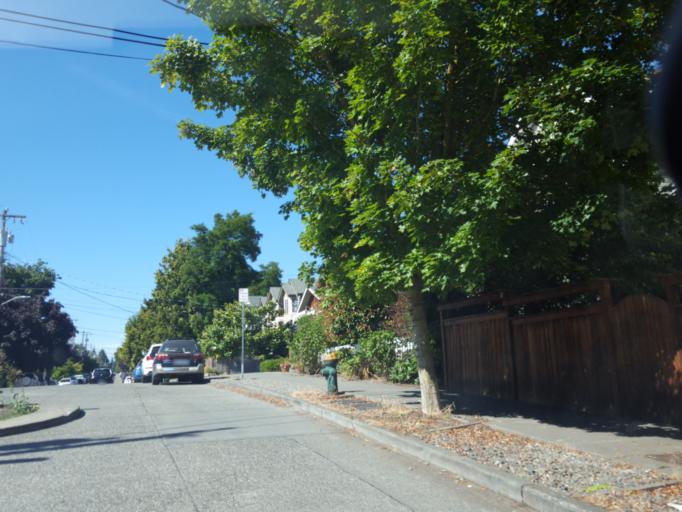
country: US
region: Washington
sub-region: King County
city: Shoreline
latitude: 47.6962
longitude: -122.3419
